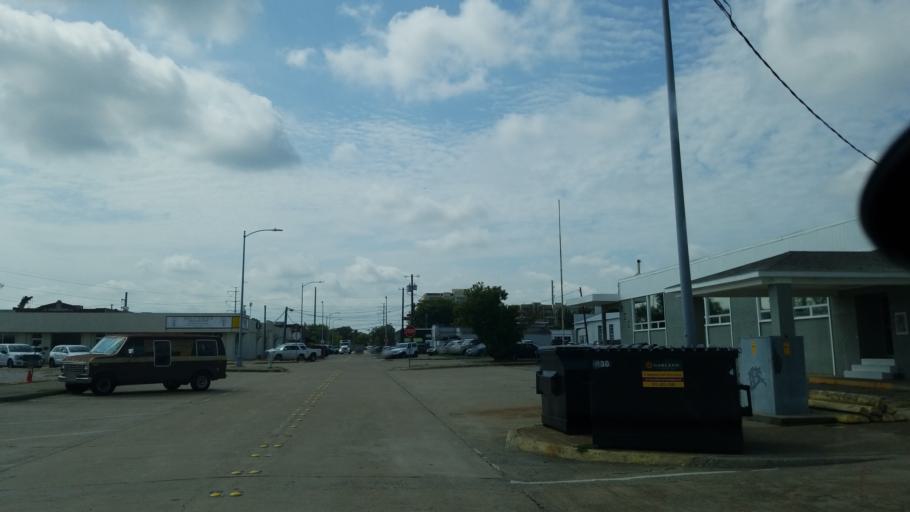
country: US
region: Texas
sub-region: Dallas County
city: Garland
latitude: 32.9139
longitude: -96.6390
